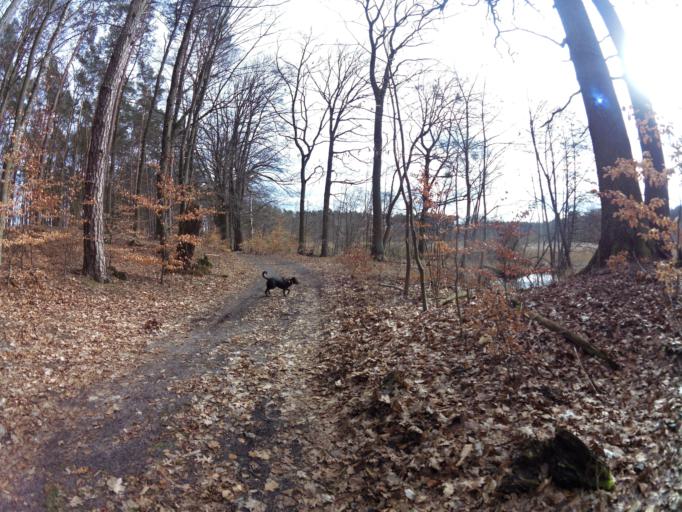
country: PL
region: Lubusz
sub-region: Powiat gorzowski
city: Lubiszyn
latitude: 52.7822
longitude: 14.8449
